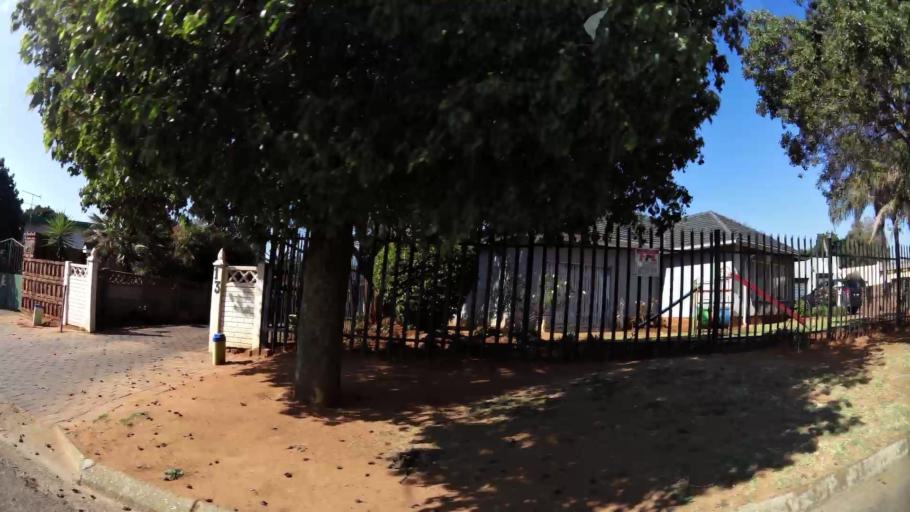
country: ZA
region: Gauteng
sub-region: City of Johannesburg Metropolitan Municipality
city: Modderfontein
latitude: -26.0522
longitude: 28.2056
